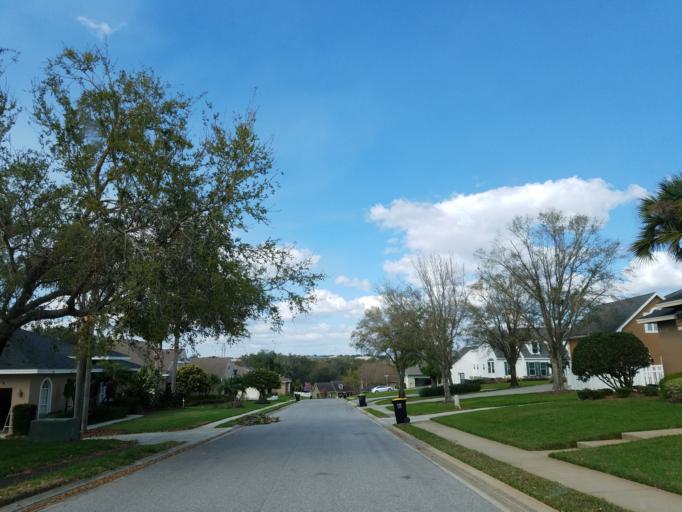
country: US
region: Florida
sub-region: Polk County
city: Lakeland Highlands
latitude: 27.9468
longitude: -81.9190
